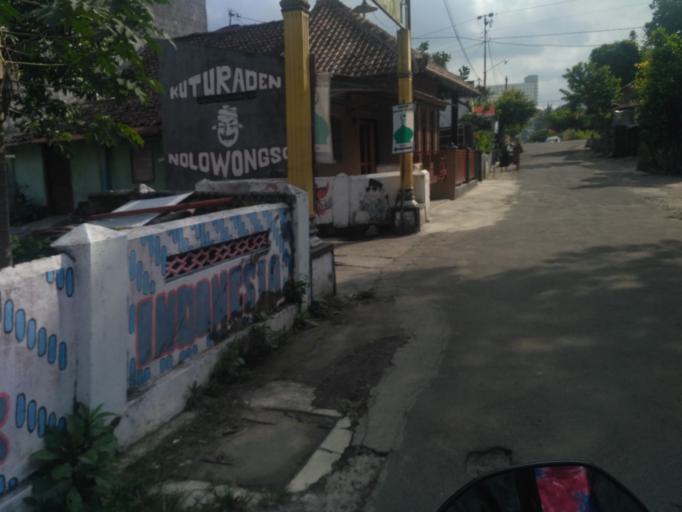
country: ID
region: Daerah Istimewa Yogyakarta
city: Yogyakarta
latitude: -7.7595
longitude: 110.3588
